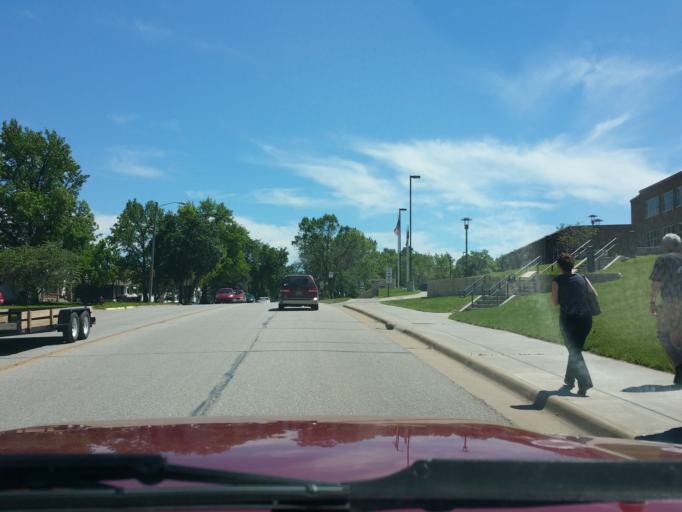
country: US
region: Kansas
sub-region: Pottawatomie County
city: Wamego
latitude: 39.2077
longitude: -96.3053
